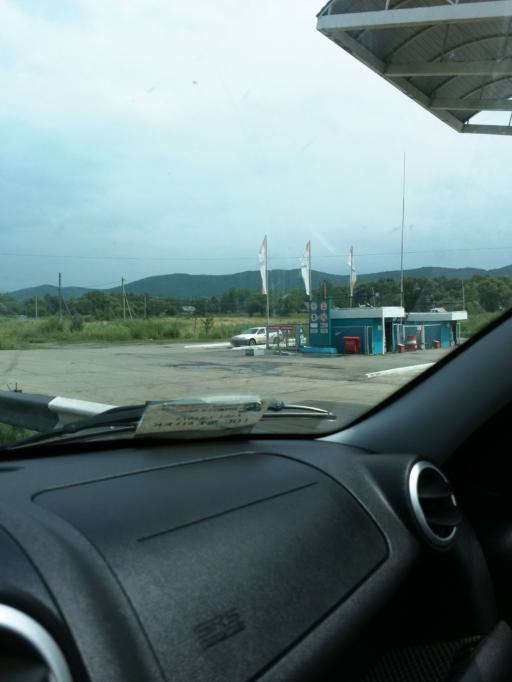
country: RU
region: Primorskiy
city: Novopokrovka
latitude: 45.8910
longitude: 134.8512
